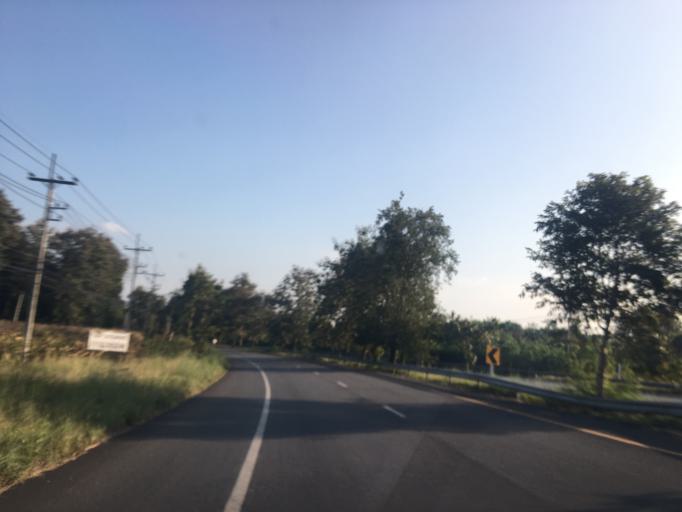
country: TH
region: Lampang
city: Ngao
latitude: 18.7894
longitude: 99.9636
